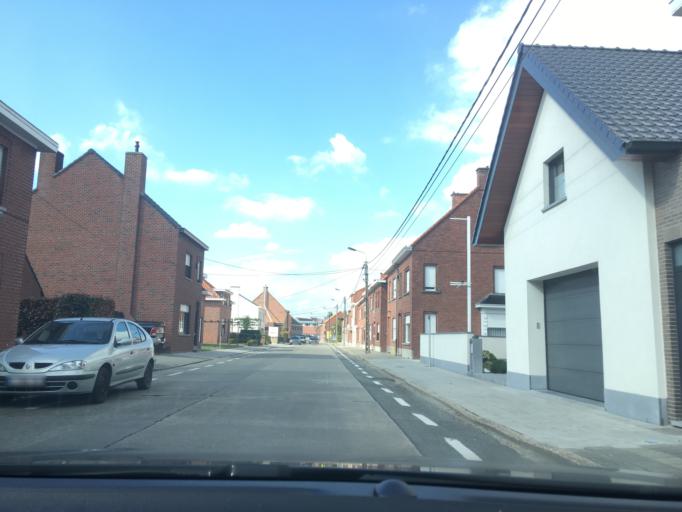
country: BE
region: Flanders
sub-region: Provincie West-Vlaanderen
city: Moorslede
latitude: 50.9356
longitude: 3.0618
